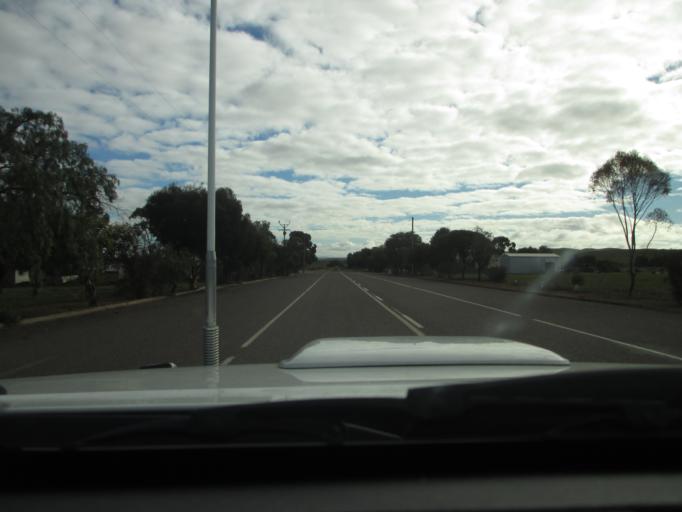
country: AU
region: South Australia
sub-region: Flinders Ranges
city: Quorn
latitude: -32.4233
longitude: 138.5304
